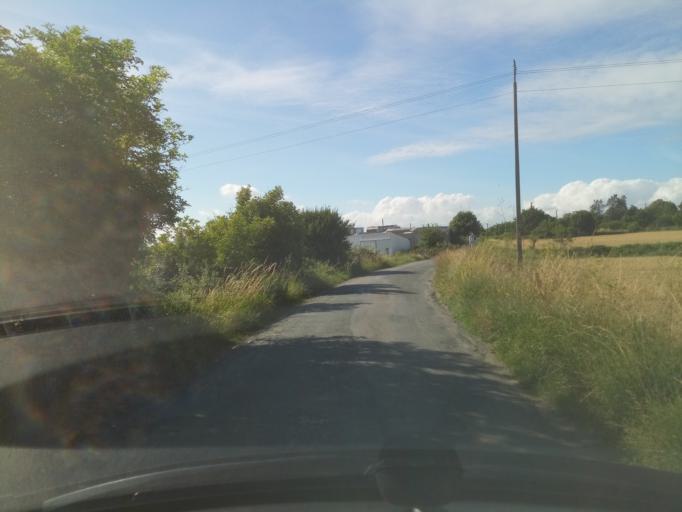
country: FR
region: Poitou-Charentes
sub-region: Departement de la Charente-Maritime
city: Marans
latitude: 46.3001
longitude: -0.9942
